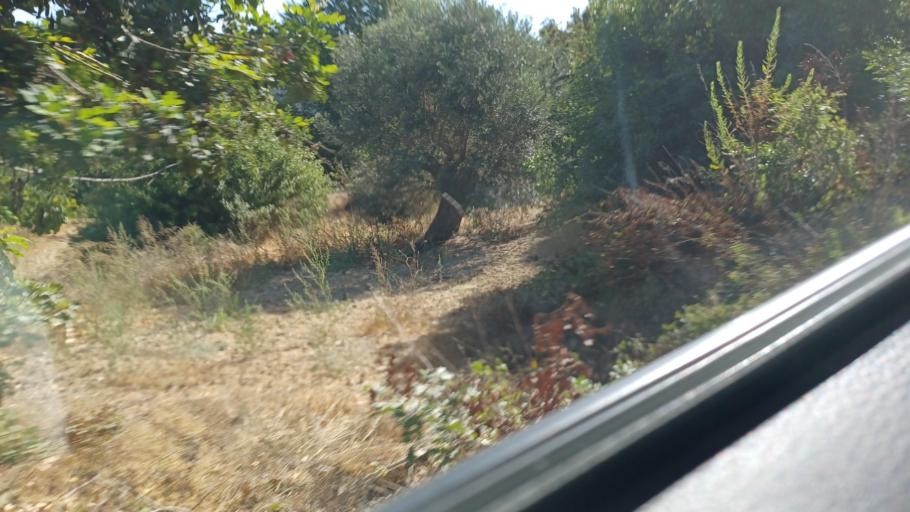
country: CY
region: Pafos
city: Tala
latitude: 34.8602
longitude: 32.4503
